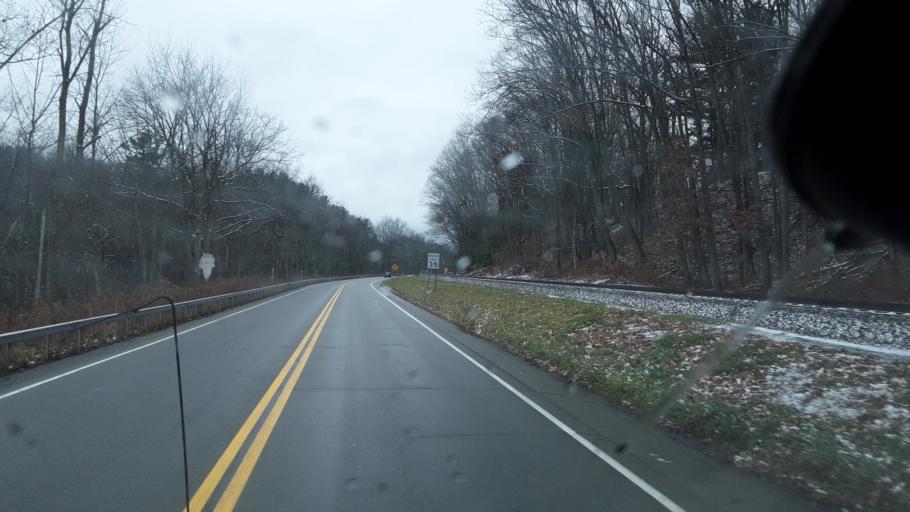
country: US
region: New York
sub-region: Cattaraugus County
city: Westons Mills
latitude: 42.0555
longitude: -78.3648
